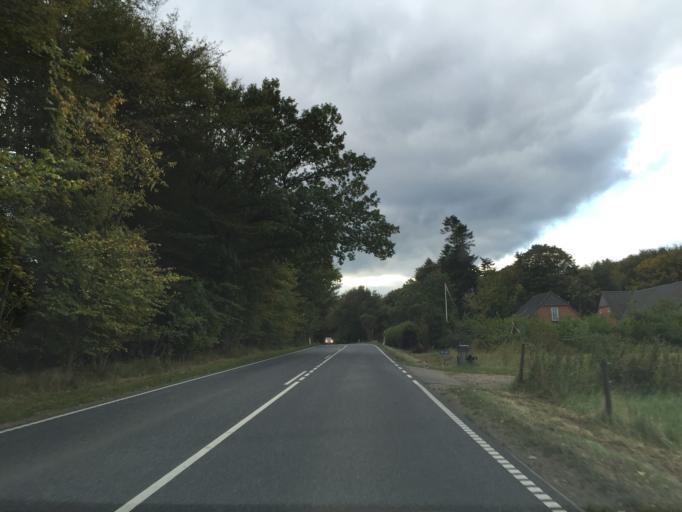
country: DK
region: Central Jutland
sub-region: Favrskov Kommune
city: Ulstrup
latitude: 56.3303
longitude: 9.8250
